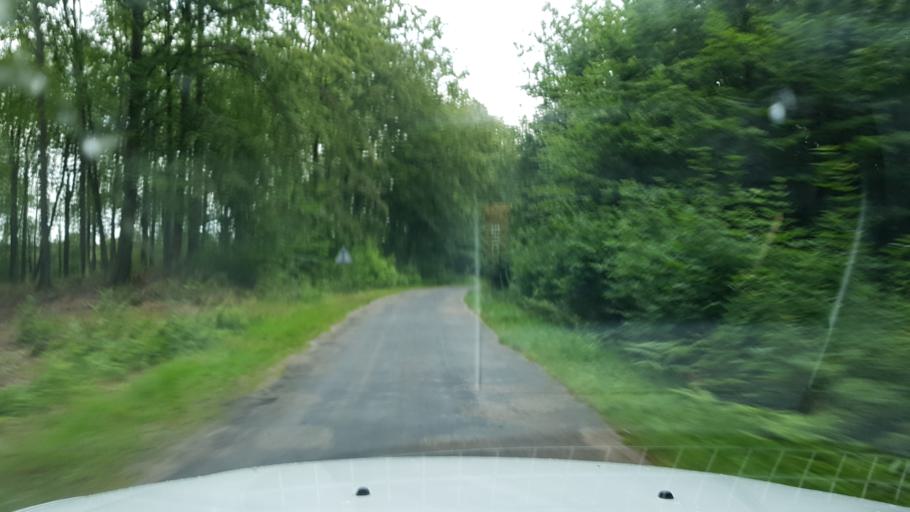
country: PL
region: West Pomeranian Voivodeship
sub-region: Powiat koszalinski
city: Bobolice
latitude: 53.8932
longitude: 16.6781
